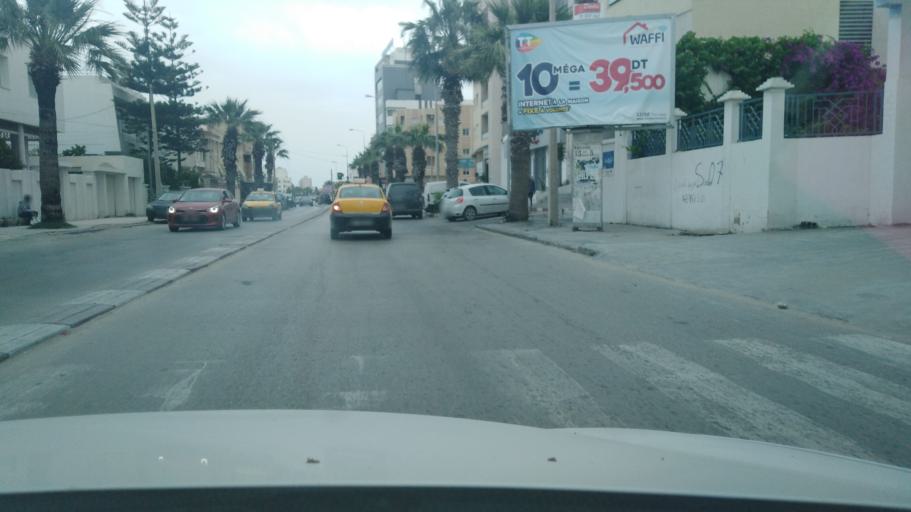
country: TN
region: Susah
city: Sousse
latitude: 35.8317
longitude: 10.6241
